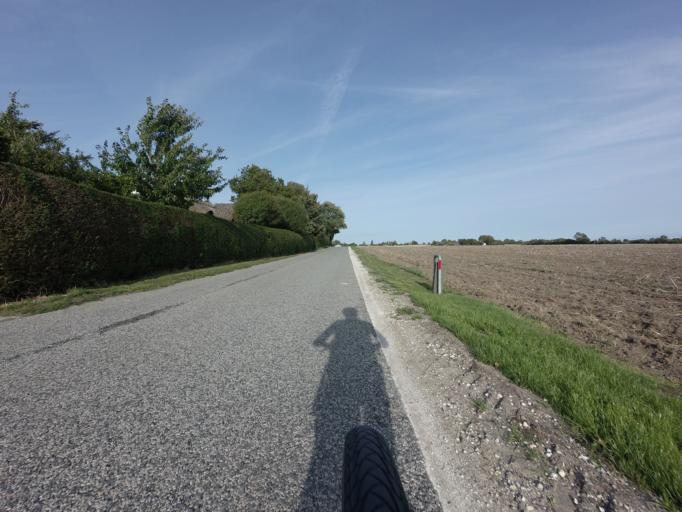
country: DK
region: Zealand
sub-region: Faxe Kommune
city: Fakse Ladeplads
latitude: 55.2515
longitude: 12.2543
